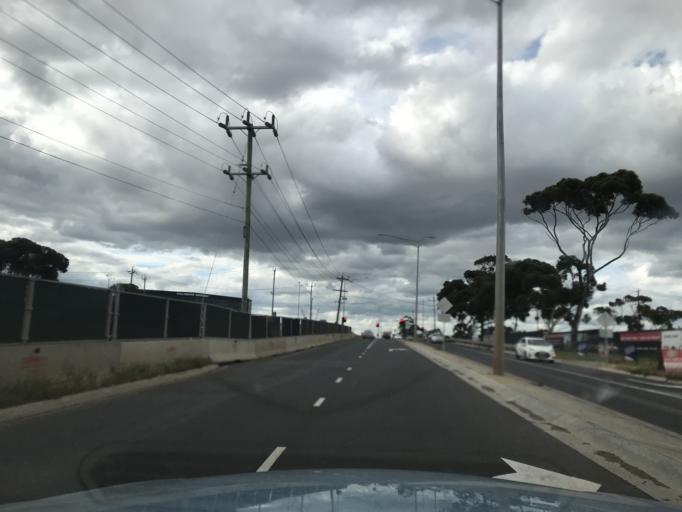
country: AU
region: Victoria
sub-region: Wyndham
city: Williams Landing
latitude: -37.8407
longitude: 144.7469
